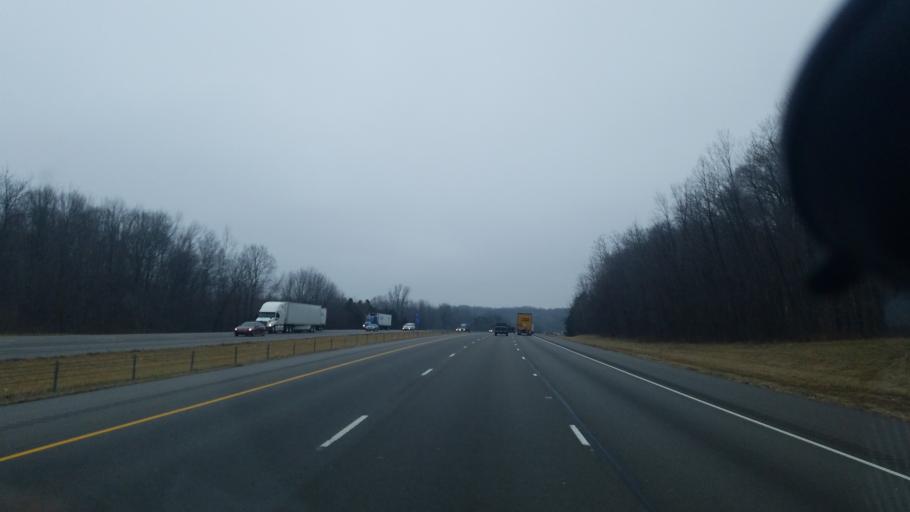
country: US
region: Ohio
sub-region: Knox County
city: Fredericktown
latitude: 40.5522
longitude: -82.6507
